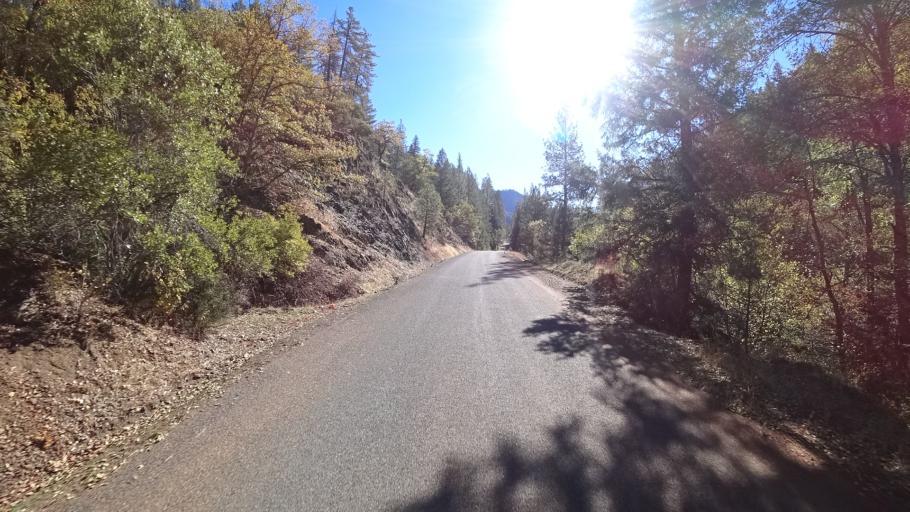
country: US
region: California
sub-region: Trinity County
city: Weaverville
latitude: 41.1472
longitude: -123.1076
